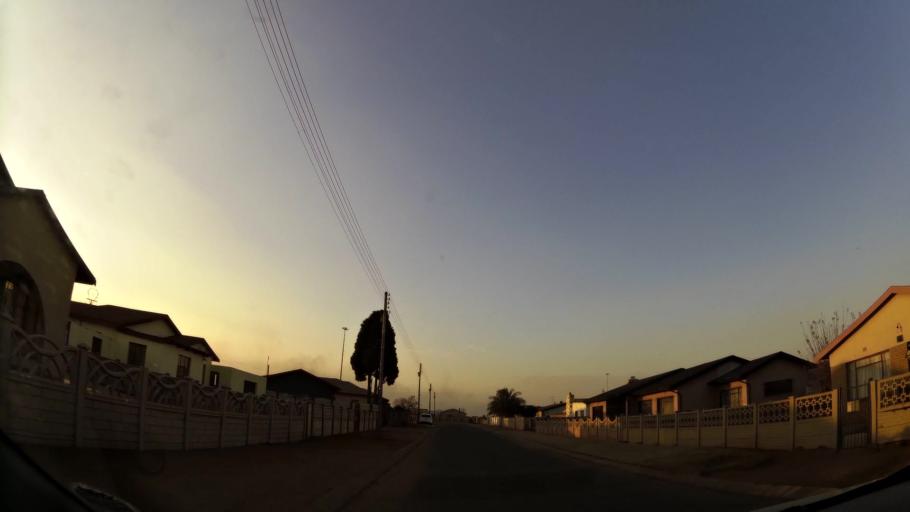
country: ZA
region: Gauteng
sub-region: West Rand District Municipality
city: Randfontein
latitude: -26.2031
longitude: 27.7083
